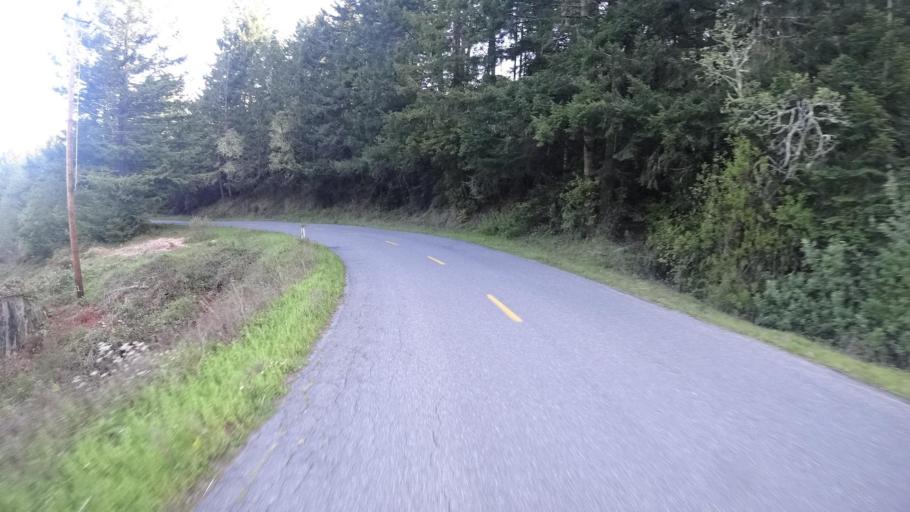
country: US
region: California
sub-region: Humboldt County
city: Bayside
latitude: 40.7591
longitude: -124.0047
